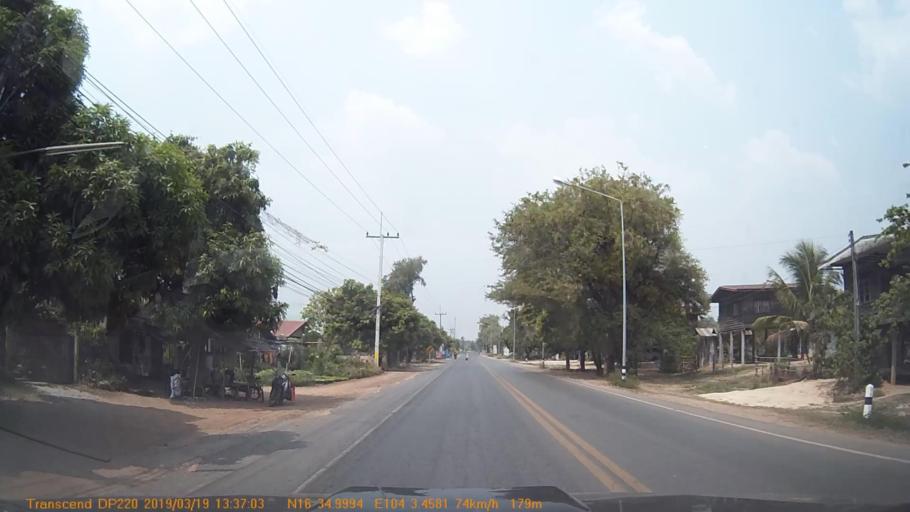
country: TH
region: Kalasin
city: Kuchinarai
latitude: 16.5838
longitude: 104.0576
